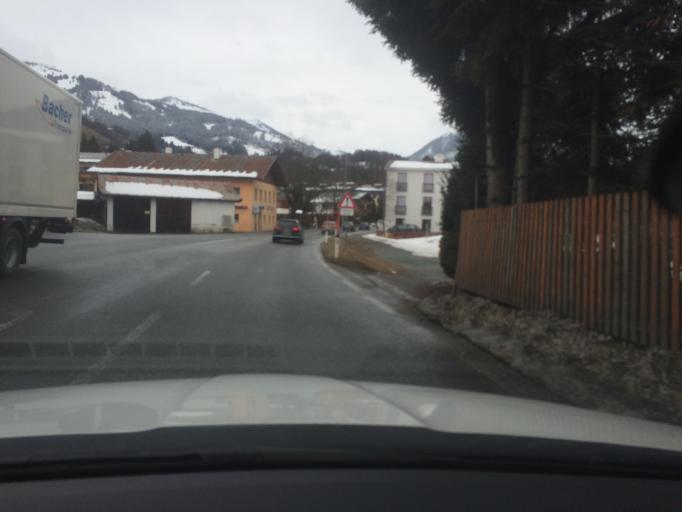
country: AT
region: Tyrol
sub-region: Politischer Bezirk Kitzbuhel
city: Kitzbuhel
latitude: 47.4369
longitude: 12.4036
